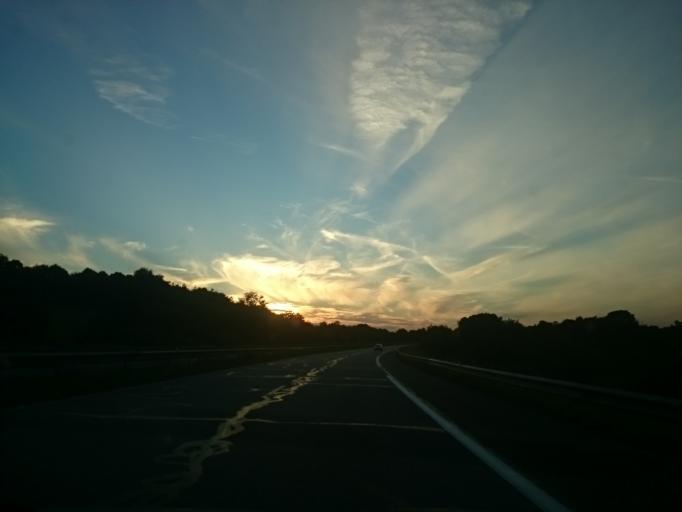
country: FR
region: Brittany
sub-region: Departement du Finistere
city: Ergue-Gaberic
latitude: 47.9894
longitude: -4.0380
